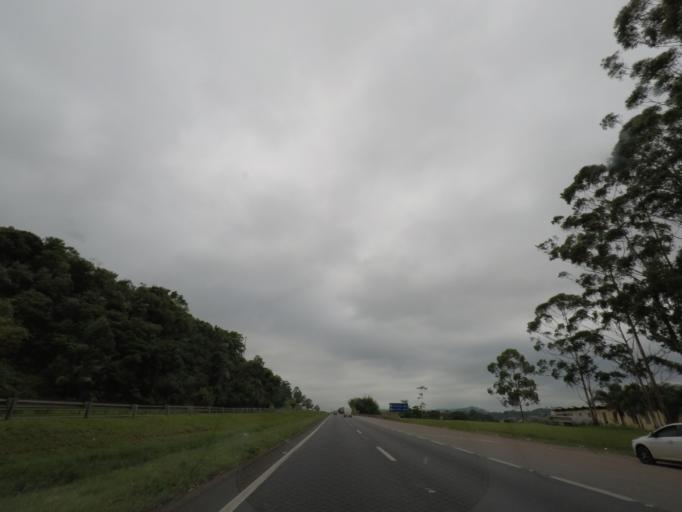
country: BR
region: Sao Paulo
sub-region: Itatiba
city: Itatiba
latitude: -22.9809
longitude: -46.8245
